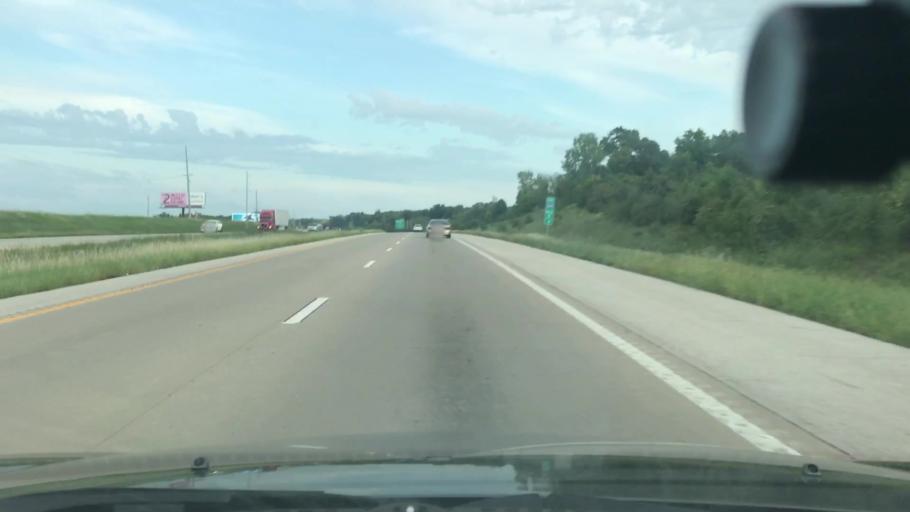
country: US
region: Missouri
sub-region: Saint Charles County
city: Weldon Spring
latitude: 38.7243
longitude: -90.7286
